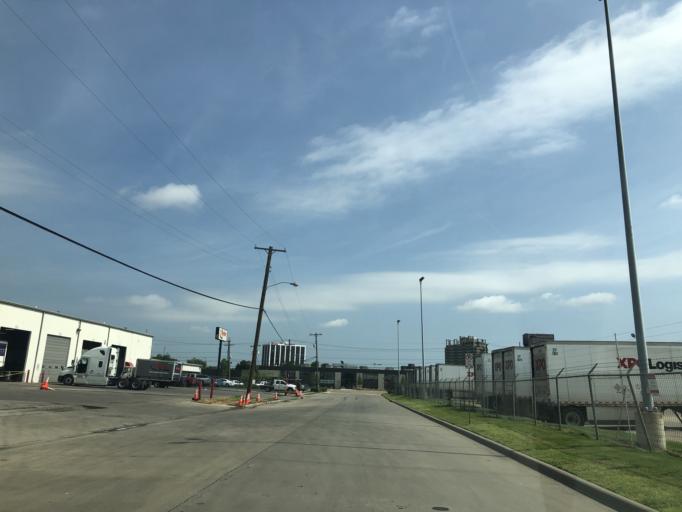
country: US
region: Texas
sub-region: Dallas County
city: Dallas
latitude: 32.8107
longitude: -96.8691
